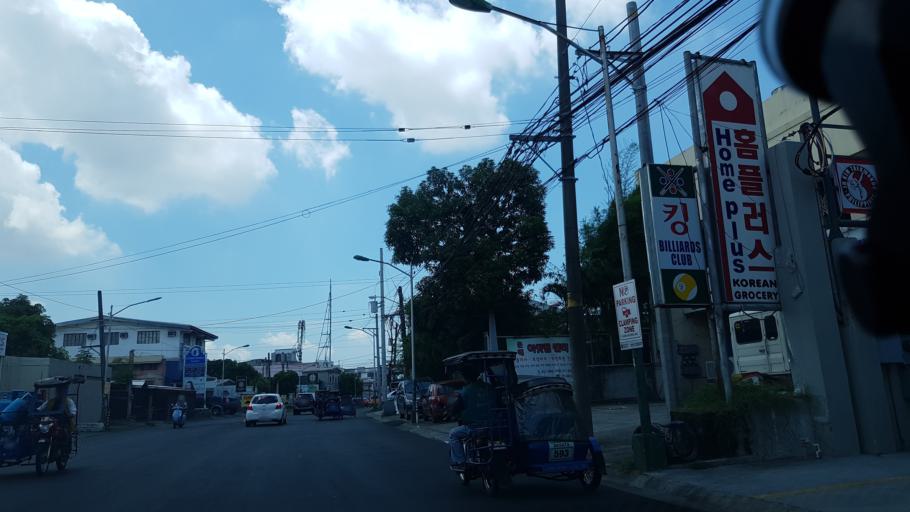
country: PH
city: Sambayanihan People's Village
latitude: 14.4460
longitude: 121.0212
